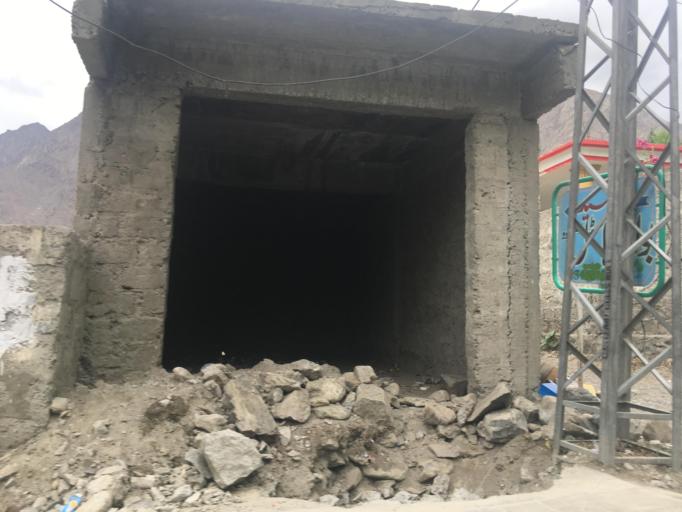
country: PK
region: Gilgit-Baltistan
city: Skardu
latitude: 35.2776
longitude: 75.6373
